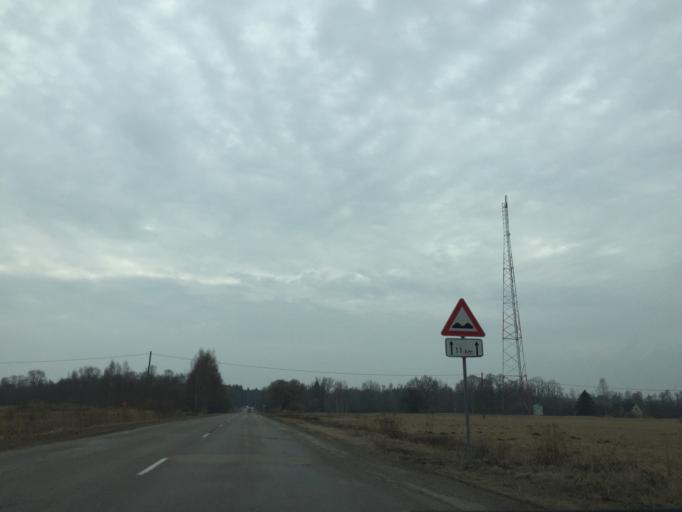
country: LV
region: Kekava
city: Balozi
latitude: 56.7719
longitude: 24.1109
